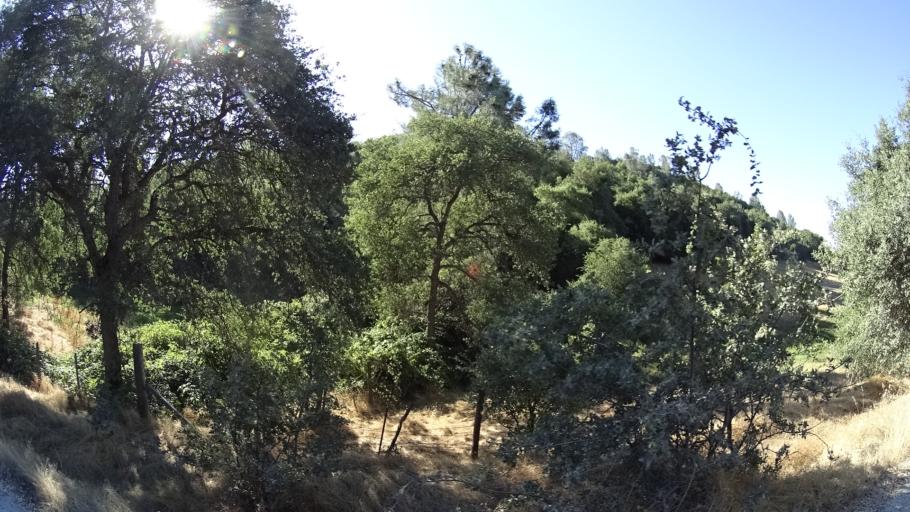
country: US
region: California
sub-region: Calaveras County
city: Angels Camp
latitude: 38.0607
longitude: -120.5034
